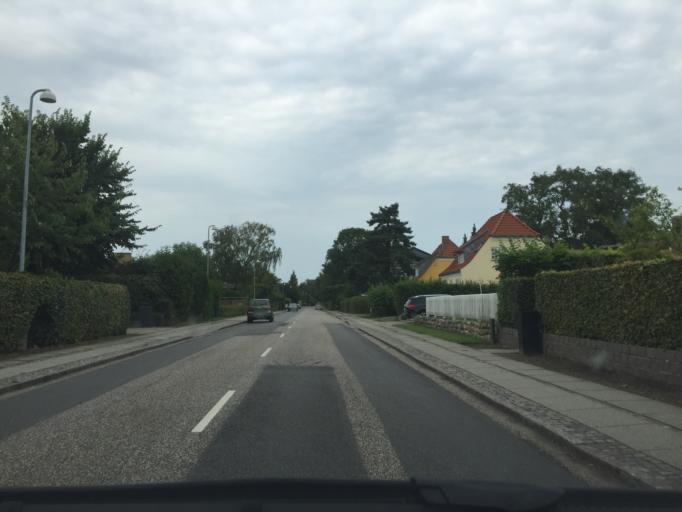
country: DK
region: Capital Region
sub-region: Lyngby-Tarbaek Kommune
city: Kongens Lyngby
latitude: 55.7827
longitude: 12.5027
